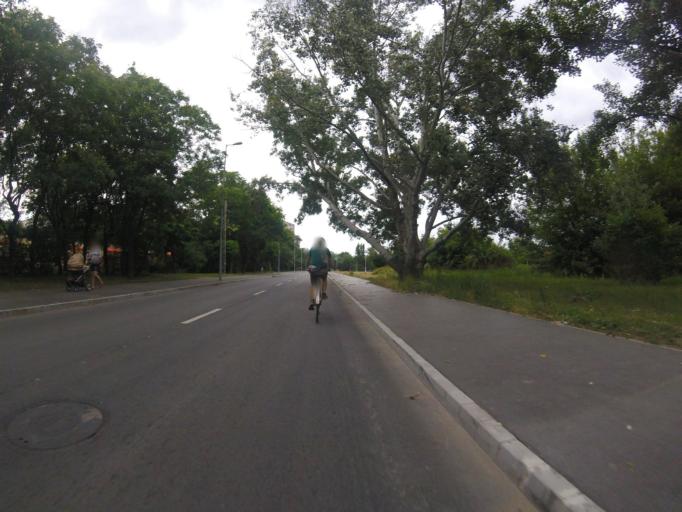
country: HU
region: Pest
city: Budakalasz
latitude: 47.6004
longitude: 19.0653
